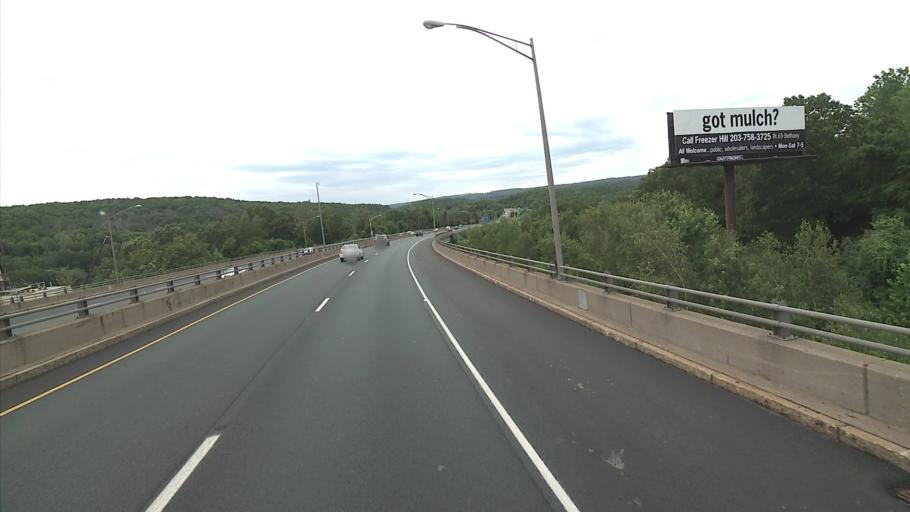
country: US
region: Connecticut
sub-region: New Haven County
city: Waterbury
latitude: 41.5248
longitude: -73.0442
